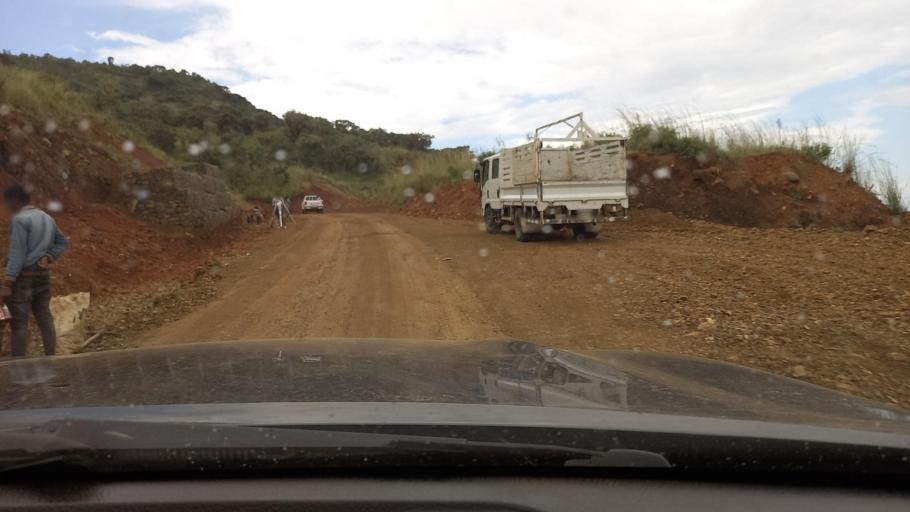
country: ET
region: Southern Nations, Nationalities, and People's Region
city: Mizan Teferi
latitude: 6.2039
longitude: 35.6607
